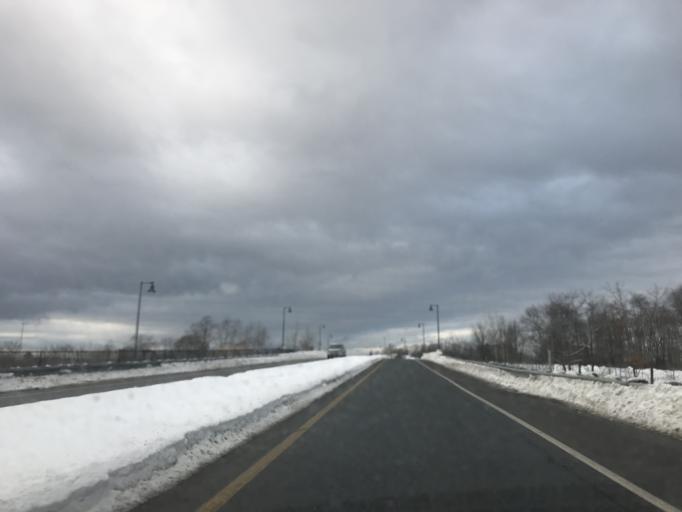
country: US
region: Maine
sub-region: Cumberland County
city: Portland
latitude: 43.6494
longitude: -70.2839
